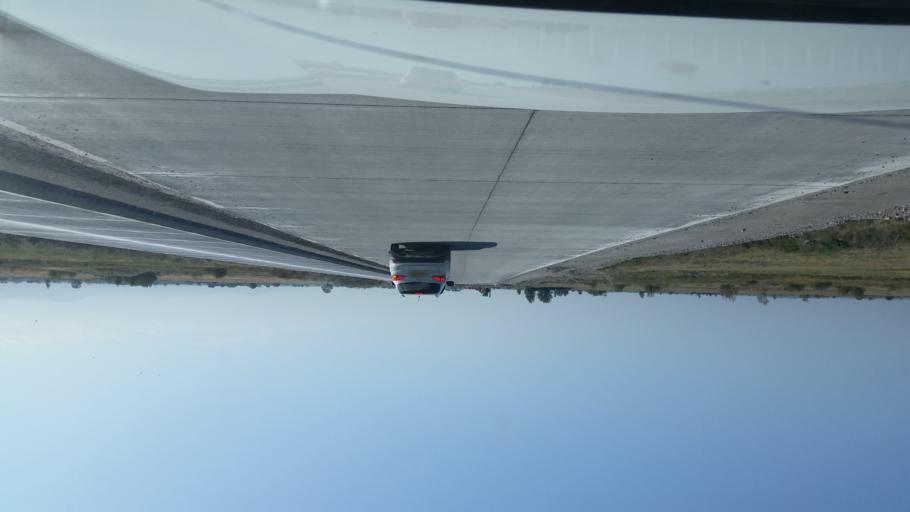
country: KZ
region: Almaty Oblysy
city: Turgen'
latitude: 43.5312
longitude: 77.6056
